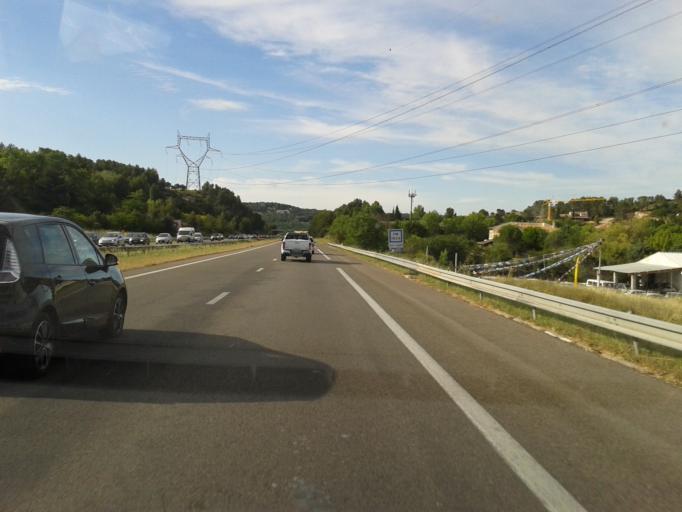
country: FR
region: Provence-Alpes-Cote d'Azur
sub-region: Departement des Bouches-du-Rhone
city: Cabries
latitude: 43.4408
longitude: 5.3963
